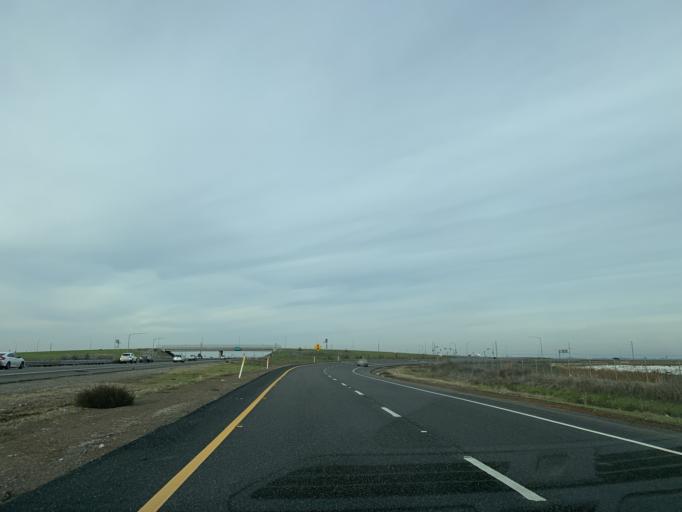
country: US
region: California
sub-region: Sacramento County
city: Elverta
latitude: 38.7103
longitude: -121.5400
